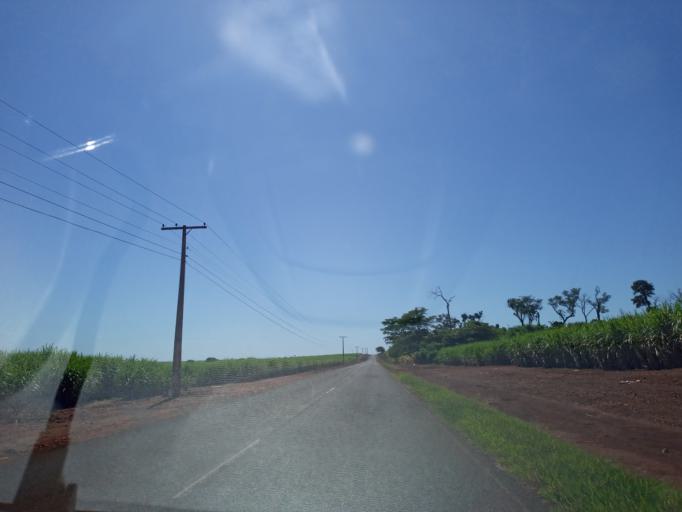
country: BR
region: Goias
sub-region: Itumbiara
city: Itumbiara
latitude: -18.4258
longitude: -49.1749
